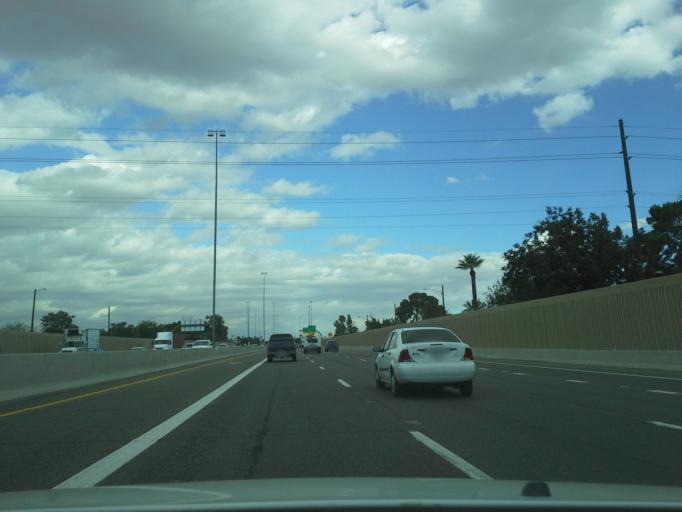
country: US
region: Arizona
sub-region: Maricopa County
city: Glendale
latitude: 33.5177
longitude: -112.1122
